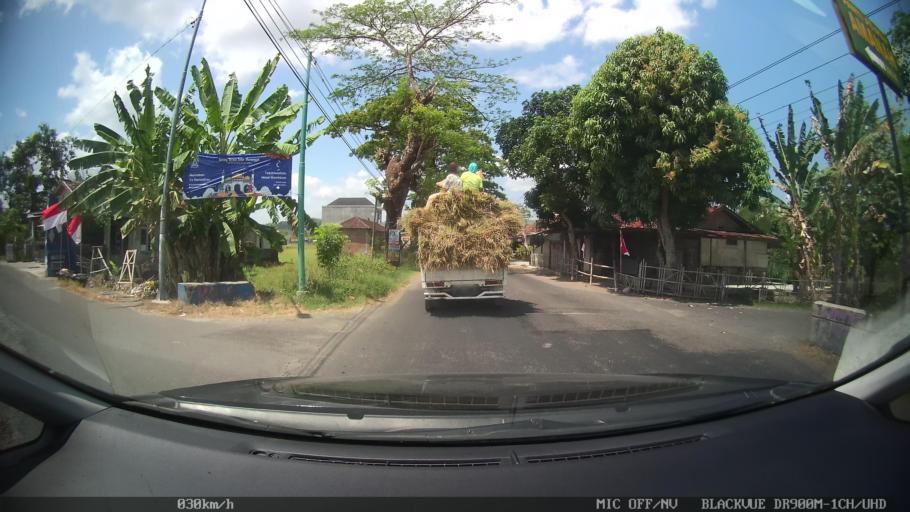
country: ID
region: Daerah Istimewa Yogyakarta
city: Sewon
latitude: -7.8982
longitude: 110.3799
